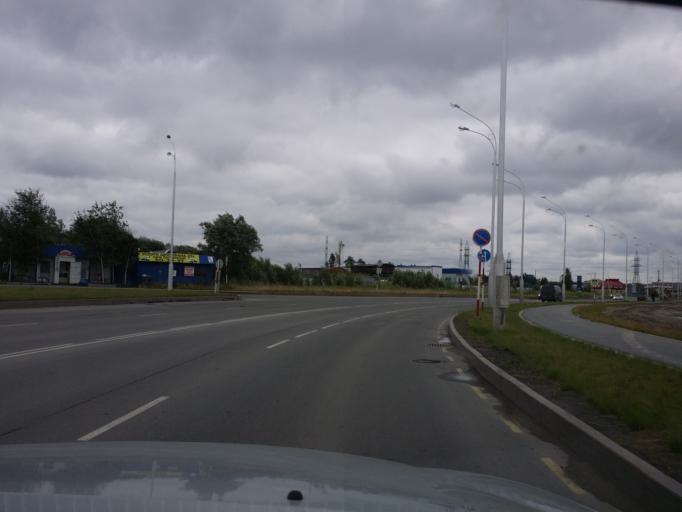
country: RU
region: Khanty-Mansiyskiy Avtonomnyy Okrug
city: Nizhnevartovsk
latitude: 60.9680
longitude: 76.5405
